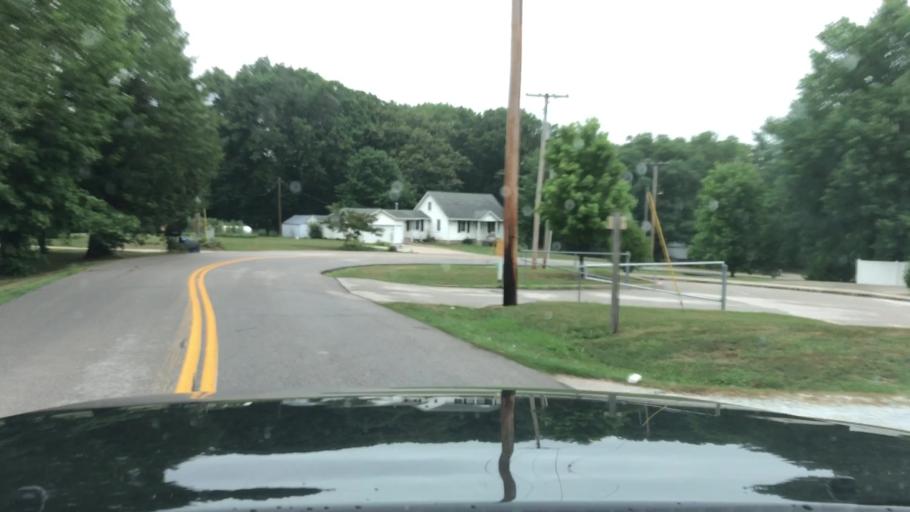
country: US
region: Missouri
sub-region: Saint Charles County
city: Wentzville
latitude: 38.8521
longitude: -90.8758
